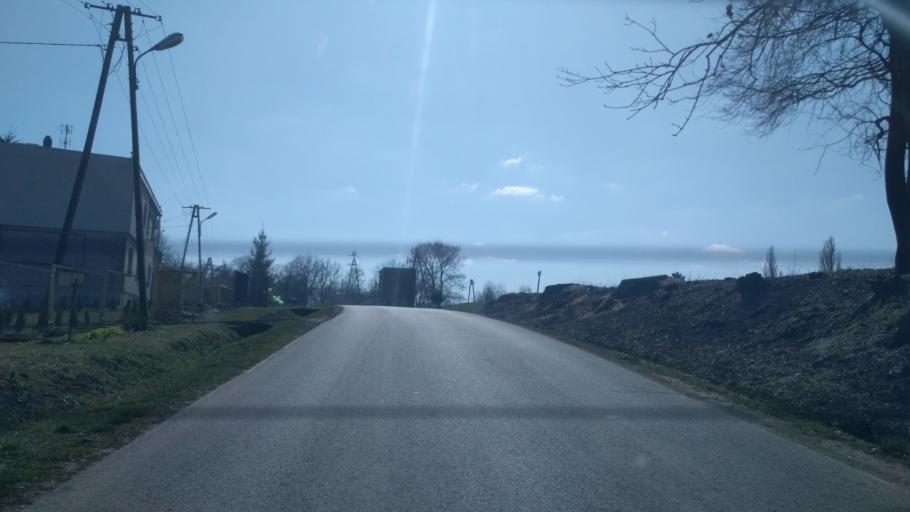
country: PL
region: Subcarpathian Voivodeship
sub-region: Powiat jaroslawski
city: Pawlosiow
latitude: 49.9552
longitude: 22.6501
